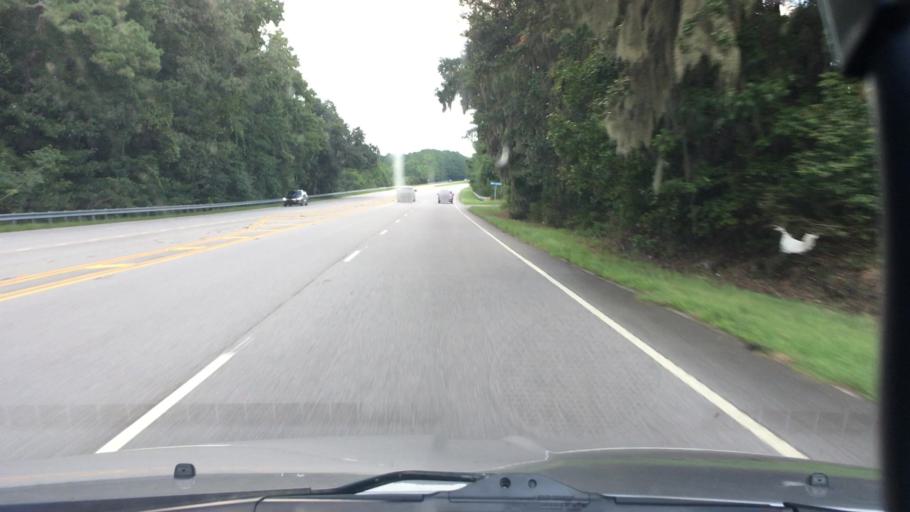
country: US
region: South Carolina
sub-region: Hampton County
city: Yemassee
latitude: 32.6267
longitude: -80.8290
